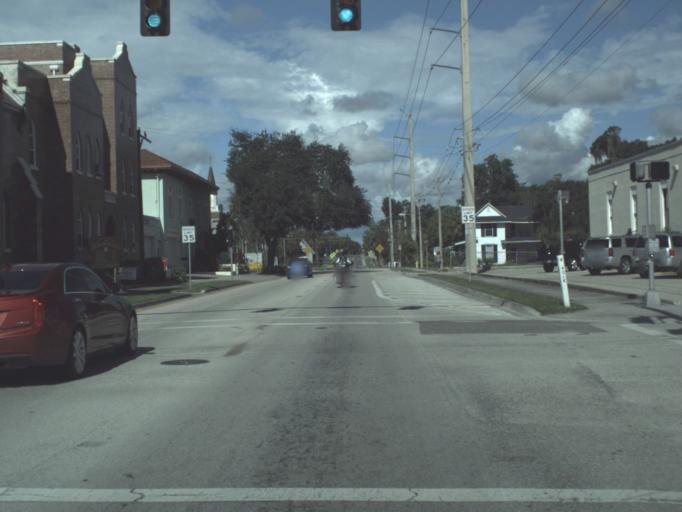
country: US
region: Florida
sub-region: DeSoto County
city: Arcadia
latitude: 27.2169
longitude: -81.8610
